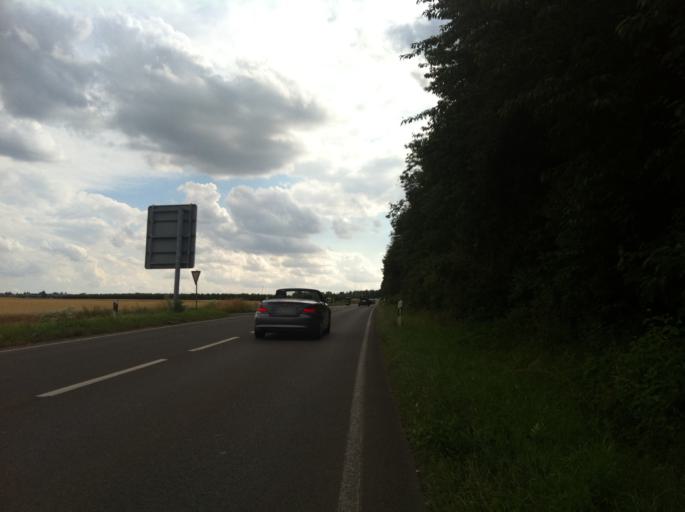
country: DE
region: Rheinland-Pfalz
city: Klein-Winternheim
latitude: 49.9553
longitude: 8.1999
